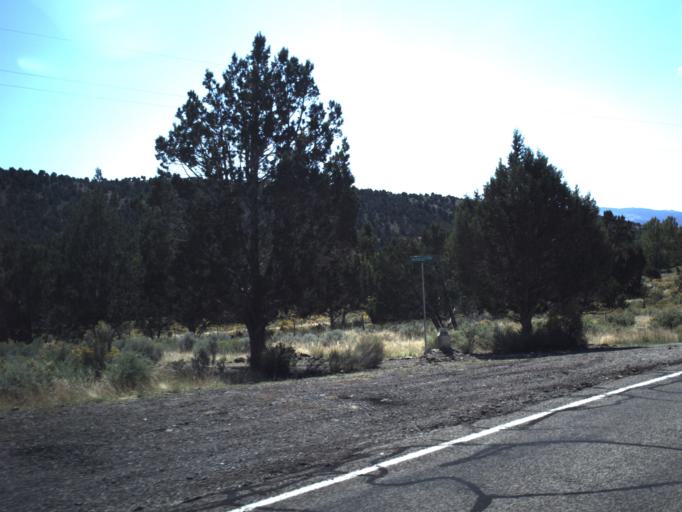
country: US
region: Utah
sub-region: Beaver County
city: Beaver
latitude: 38.2825
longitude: -112.5863
